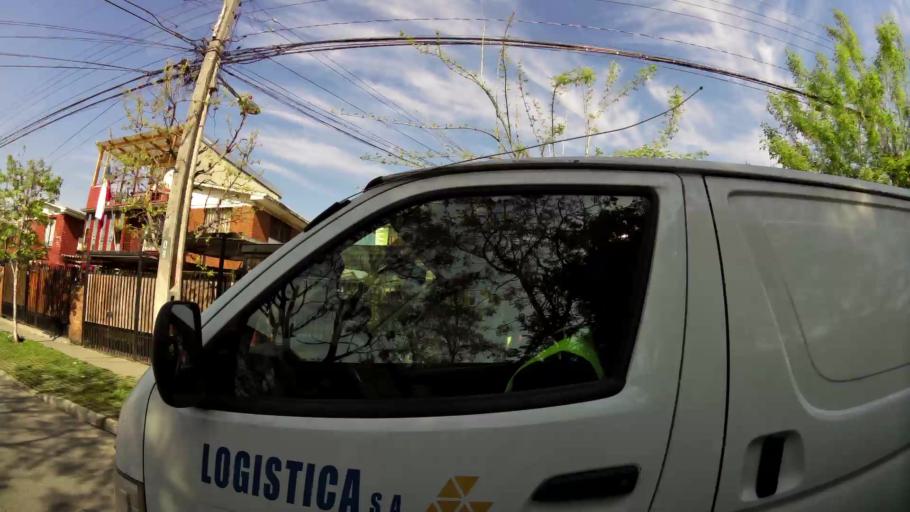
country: CL
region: Santiago Metropolitan
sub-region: Provincia de Santiago
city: La Pintana
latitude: -33.5566
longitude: -70.6002
